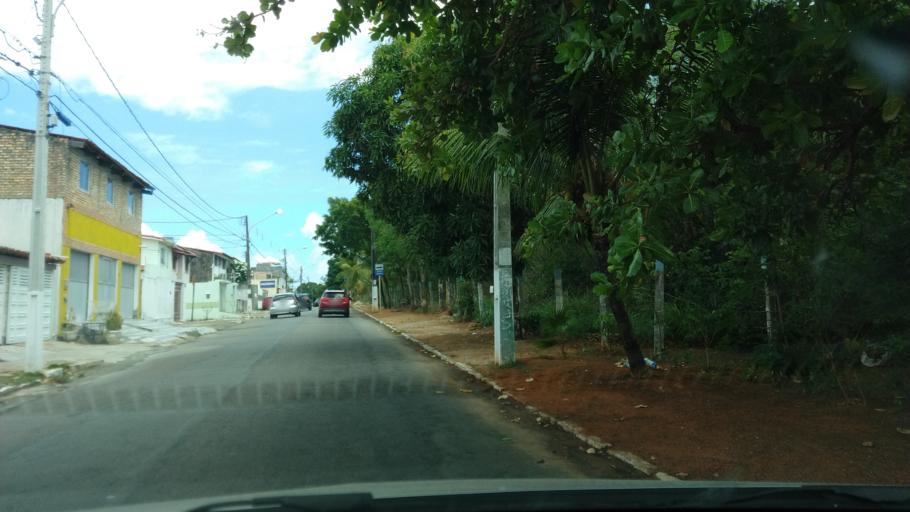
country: BR
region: Rio Grande do Norte
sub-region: Natal
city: Natal
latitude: -5.8523
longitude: -35.1992
